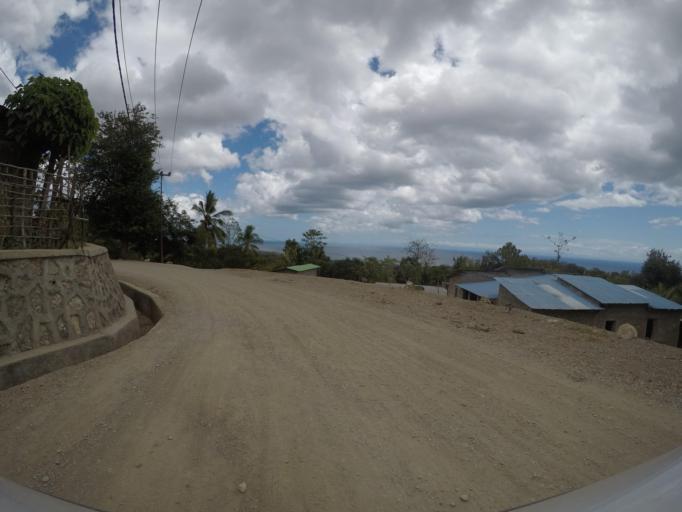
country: TL
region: Lautem
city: Lospalos
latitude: -8.3784
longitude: 126.9243
